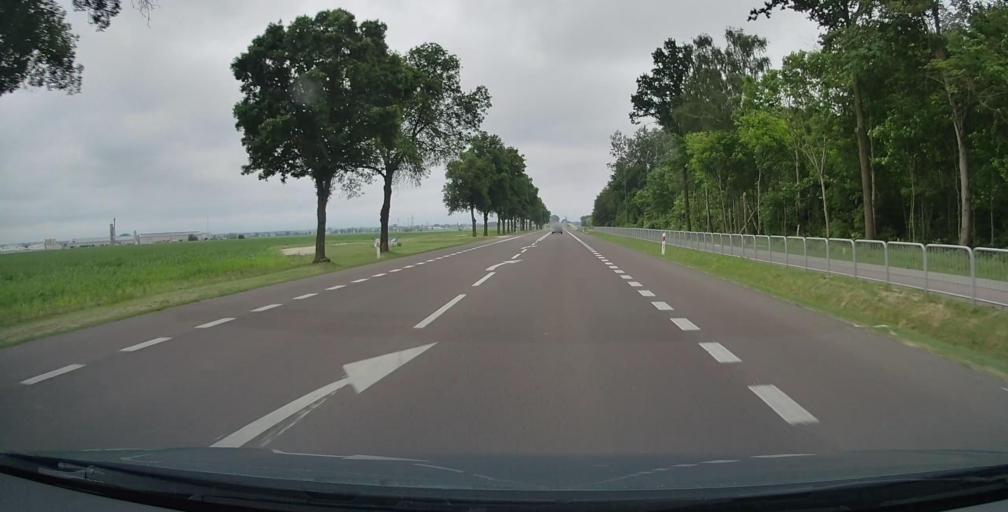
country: PL
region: Lublin Voivodeship
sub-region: Powiat bialski
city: Miedzyrzec Podlaski
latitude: 52.0096
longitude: 22.7422
